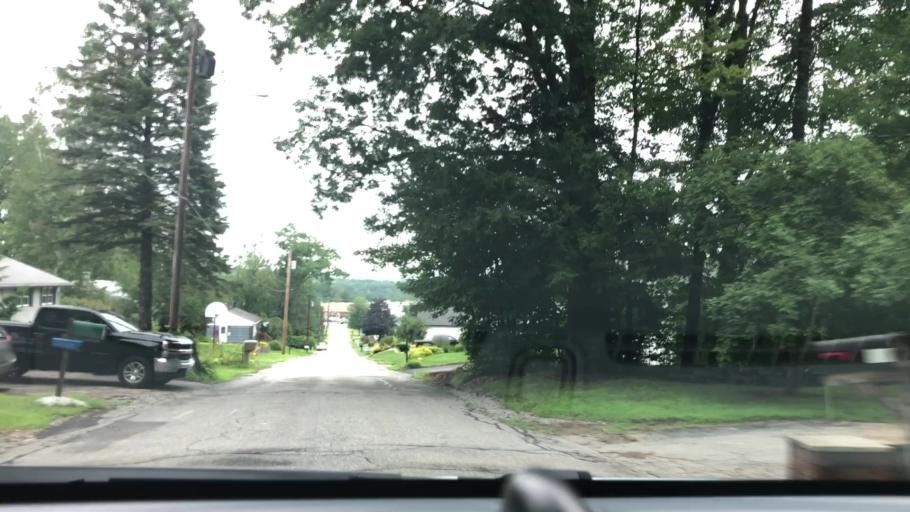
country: US
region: New Hampshire
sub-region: Hillsborough County
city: Pinardville
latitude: 42.9951
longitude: -71.5156
